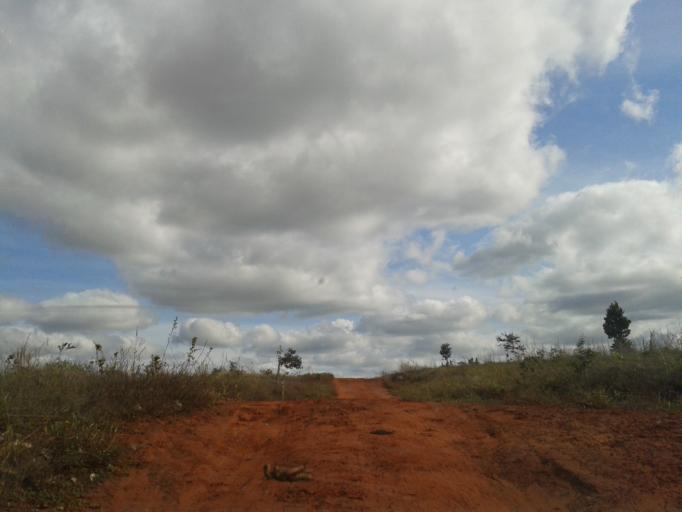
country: BR
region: Minas Gerais
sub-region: Campina Verde
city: Campina Verde
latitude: -19.4360
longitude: -49.7248
